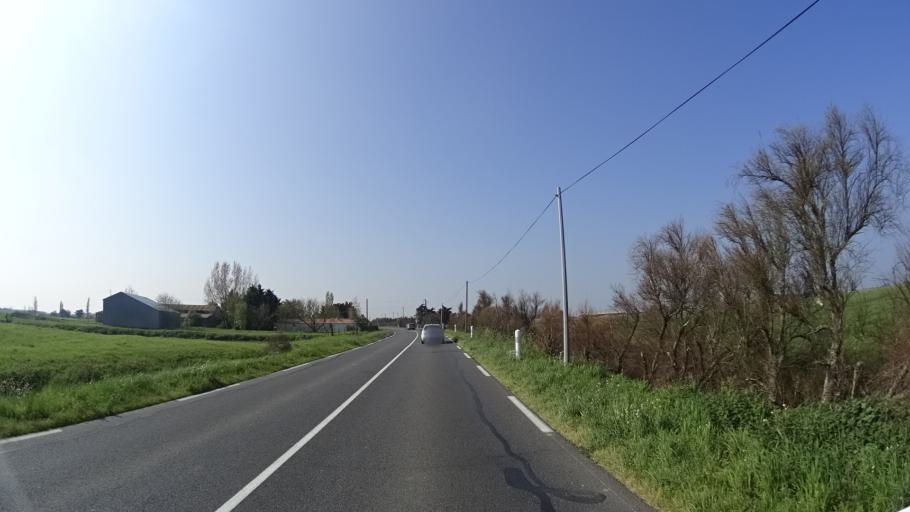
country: FR
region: Pays de la Loire
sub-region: Departement de la Vendee
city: Bouin
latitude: 46.9993
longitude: -1.9655
